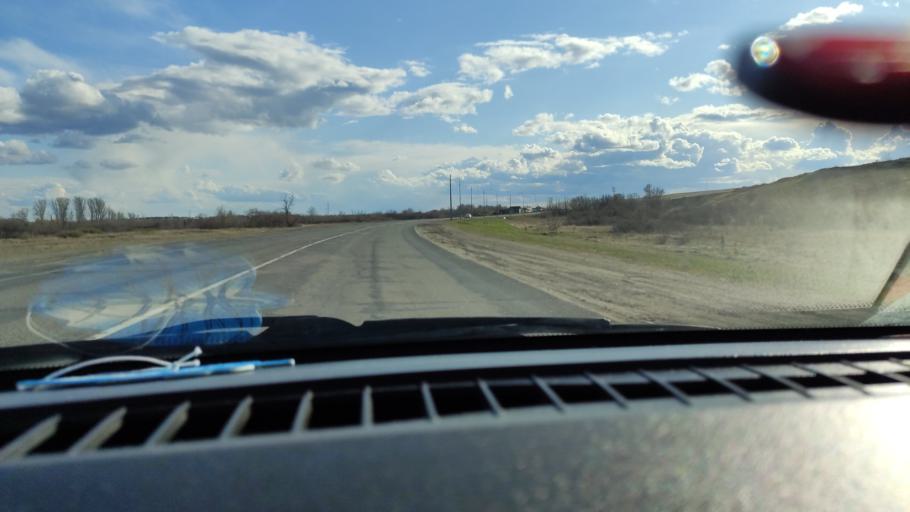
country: RU
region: Saratov
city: Sinodskoye
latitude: 52.0883
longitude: 46.8062
